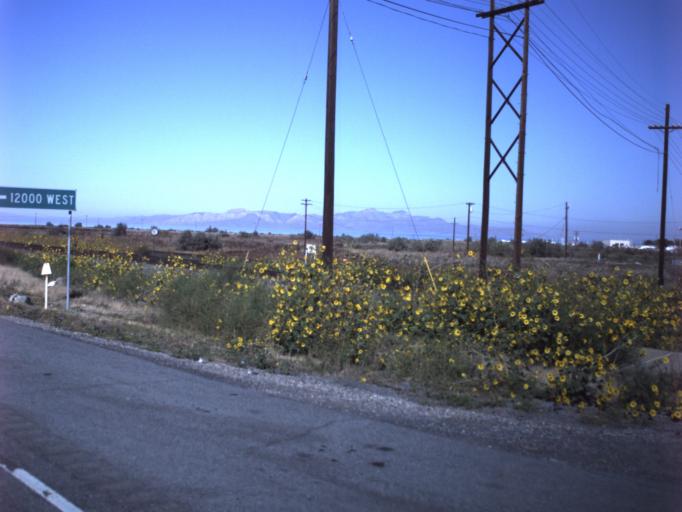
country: US
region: Utah
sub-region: Salt Lake County
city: Magna
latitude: 40.7263
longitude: -112.2016
